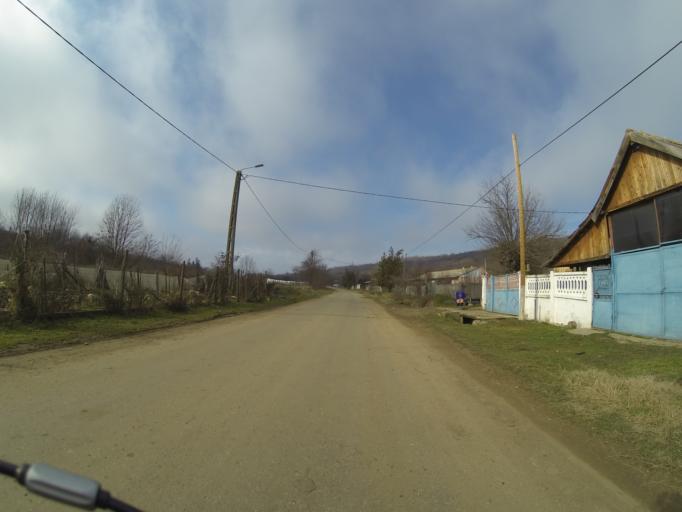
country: RO
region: Mehedinti
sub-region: Comuna Poroina Mare
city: Poroina Mare
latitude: 44.4935
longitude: 22.9974
